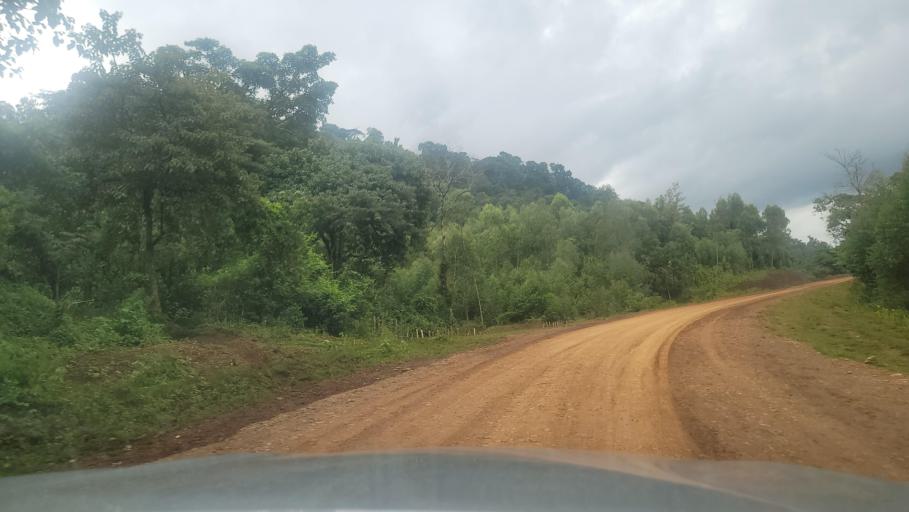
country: ET
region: Oromiya
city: Agaro
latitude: 7.7948
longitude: 36.3694
